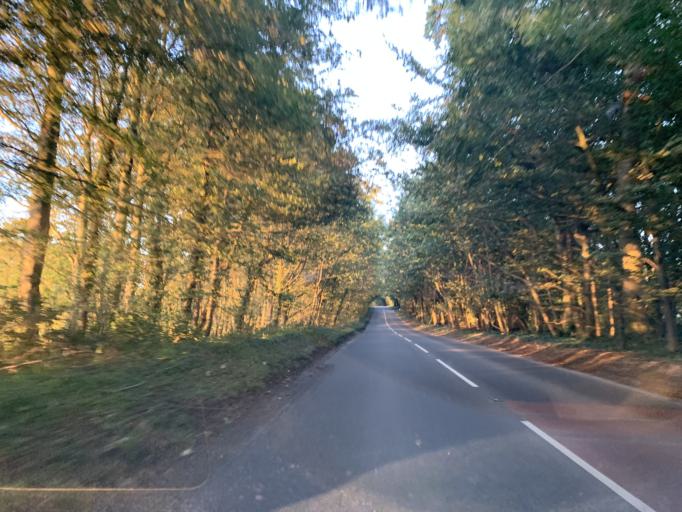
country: GB
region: England
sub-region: Wiltshire
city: Wilton
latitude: 51.0885
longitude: -1.8497
